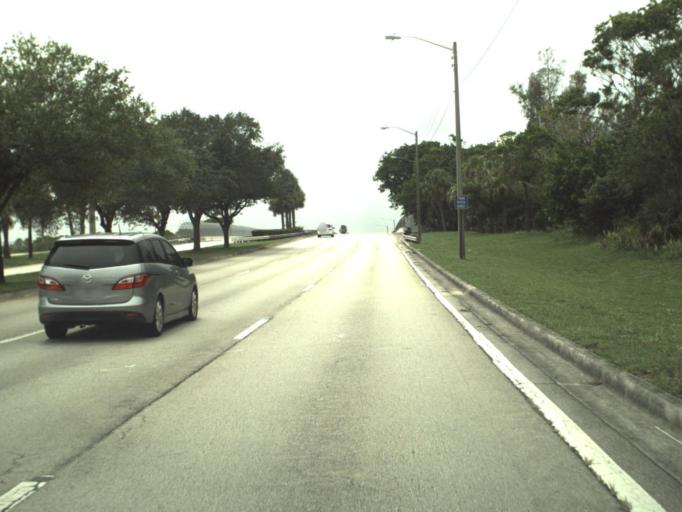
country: US
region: Florida
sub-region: Palm Beach County
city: Boca Pointe
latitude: 26.3504
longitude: -80.1682
